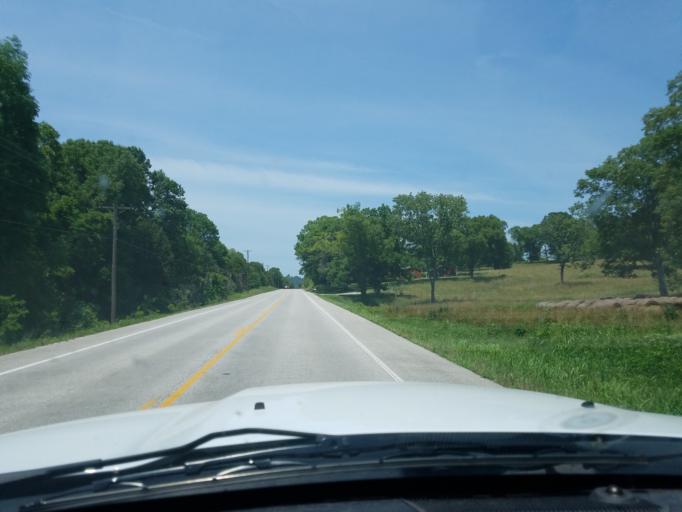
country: US
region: Tennessee
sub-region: Trousdale County
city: Hartsville
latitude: 36.4358
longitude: -86.2666
